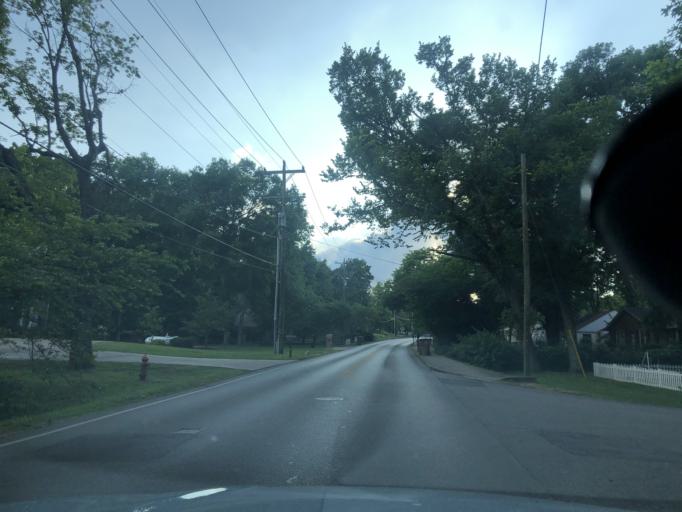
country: US
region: Tennessee
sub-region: Davidson County
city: Oak Hill
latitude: 36.1017
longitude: -86.8058
